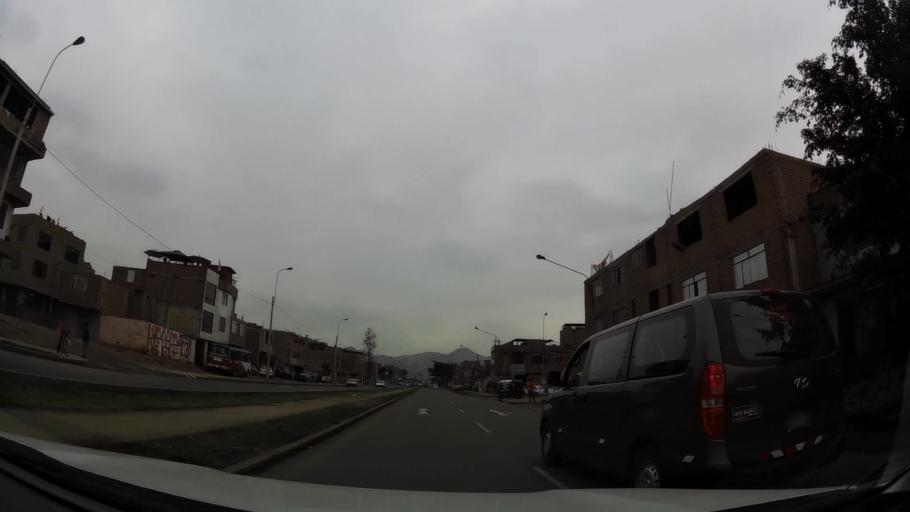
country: PE
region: Lima
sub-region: Lima
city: Vitarte
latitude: -12.0411
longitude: -76.9635
